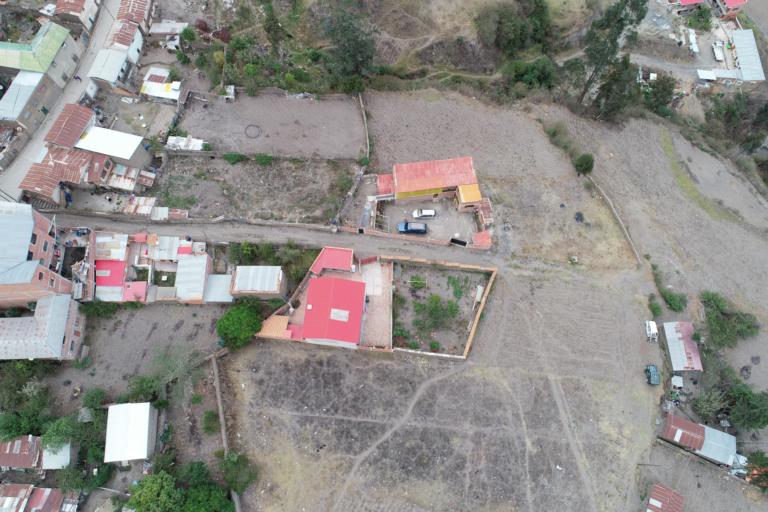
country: BO
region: La Paz
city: Sorata
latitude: -15.6337
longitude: -68.7041
